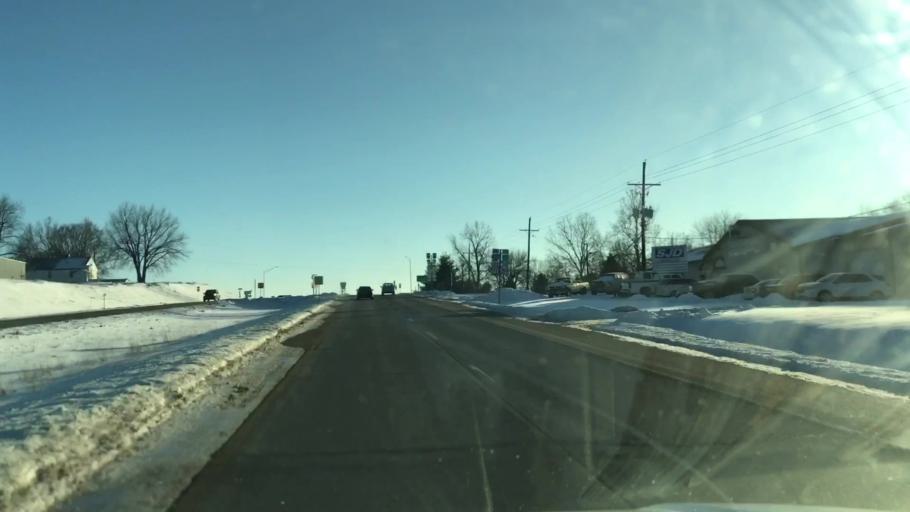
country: US
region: Missouri
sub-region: Andrew County
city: Country Club Village
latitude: 39.8621
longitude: -94.8095
